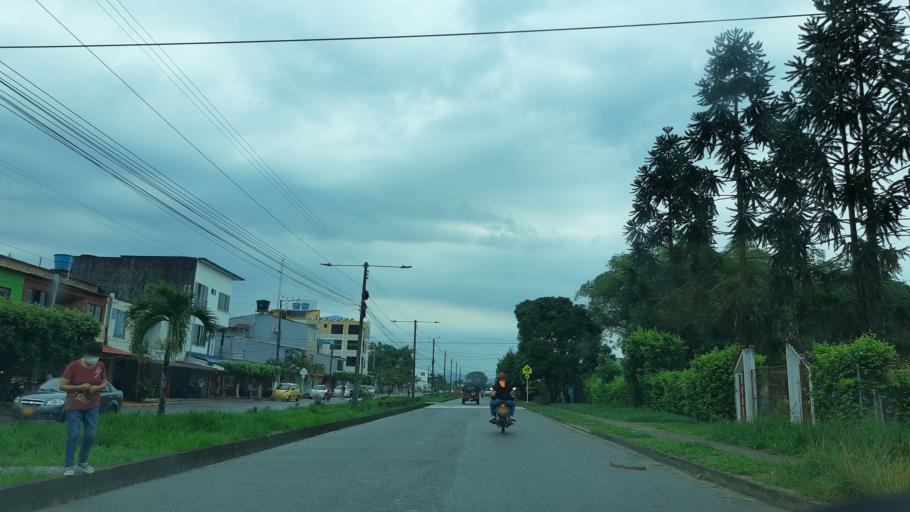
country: CO
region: Casanare
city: Monterrey
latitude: 4.8822
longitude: -72.8945
